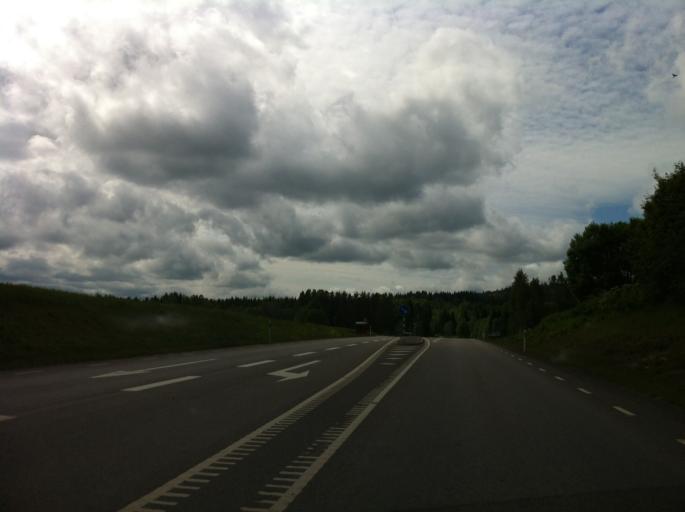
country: SE
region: Vaermland
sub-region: Sunne Kommun
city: Sunne
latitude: 59.7906
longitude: 13.0968
